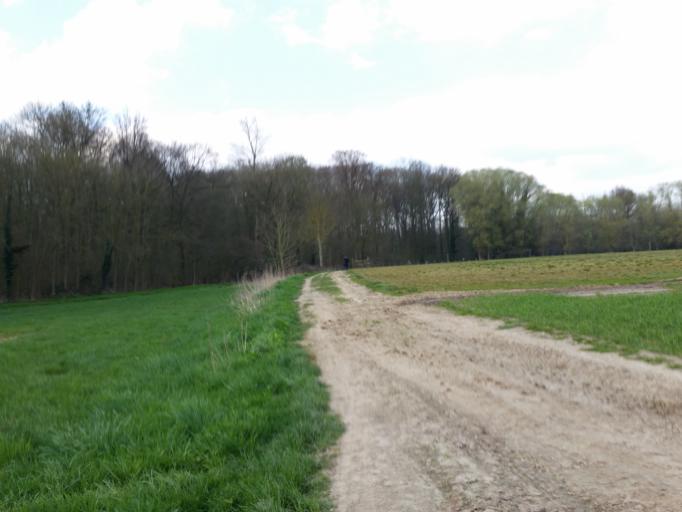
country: BE
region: Flanders
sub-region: Provincie Vlaams-Brabant
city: Steenokkerzeel
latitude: 50.9525
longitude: 4.5173
